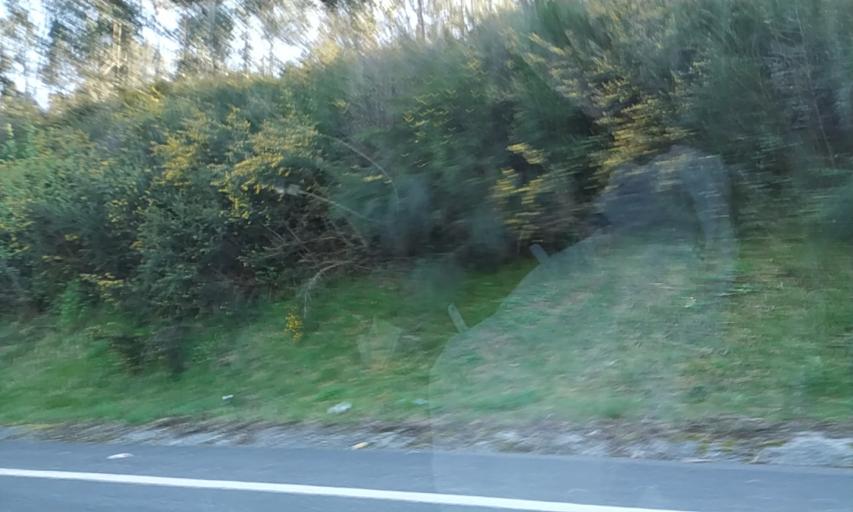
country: ES
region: Galicia
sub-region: Provincia da Coruna
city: Coiros
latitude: 43.2594
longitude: -8.1868
